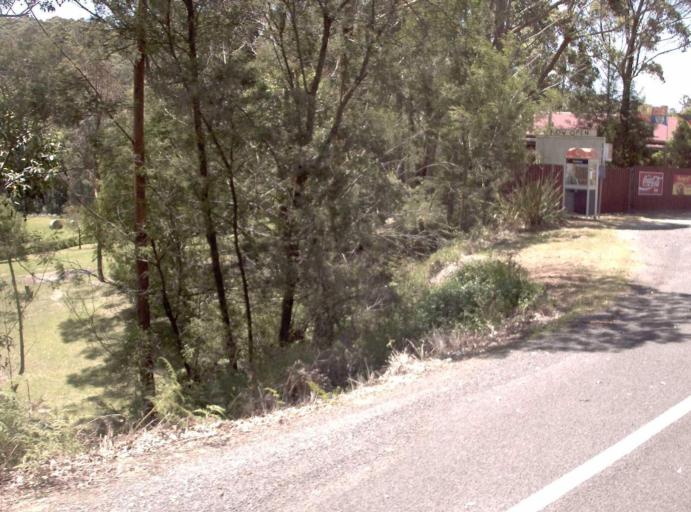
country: AU
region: Victoria
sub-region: East Gippsland
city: Lakes Entrance
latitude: -37.6983
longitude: 148.7199
